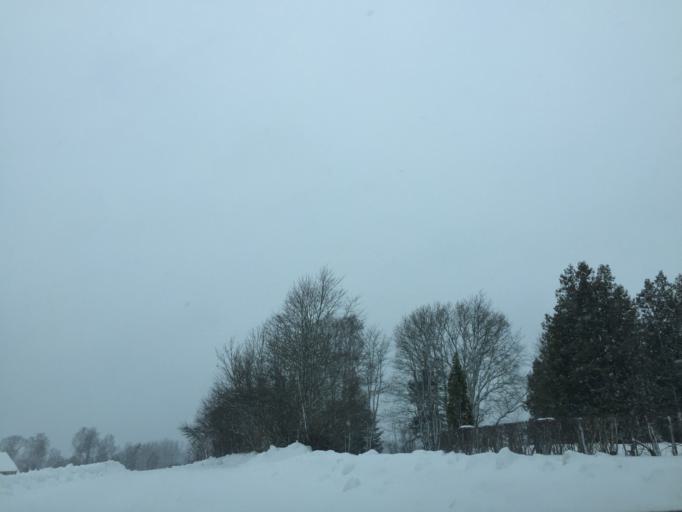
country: LV
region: Amatas Novads
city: Drabesi
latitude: 57.1694
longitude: 25.3139
